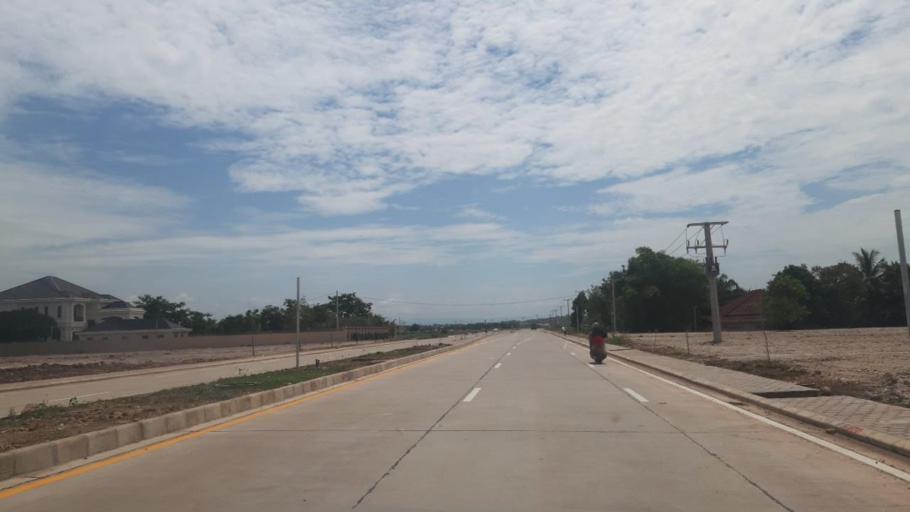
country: LA
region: Vientiane
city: Vientiane
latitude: 18.0267
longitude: 102.6038
